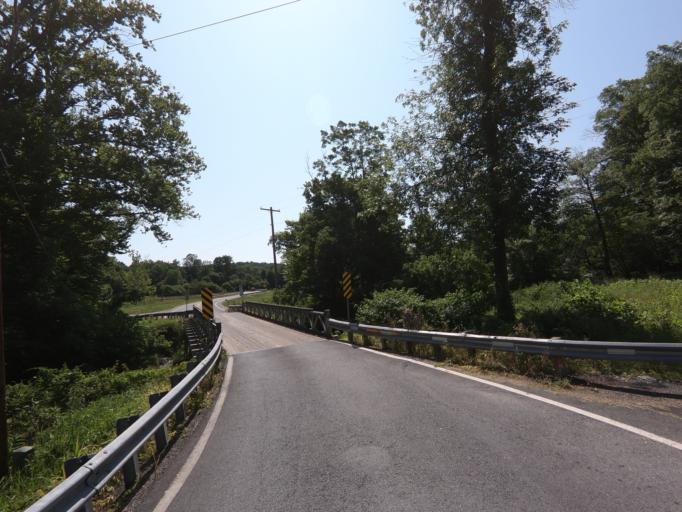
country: US
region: Maryland
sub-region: Frederick County
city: Urbana
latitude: 39.3620
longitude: -77.3271
